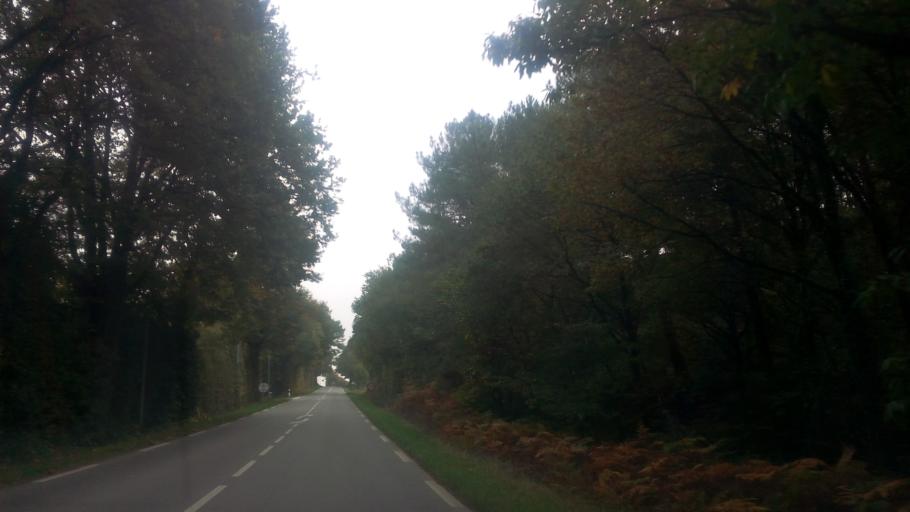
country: FR
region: Pays de la Loire
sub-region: Departement de la Loire-Atlantique
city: Avessac
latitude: 47.6366
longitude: -1.9172
